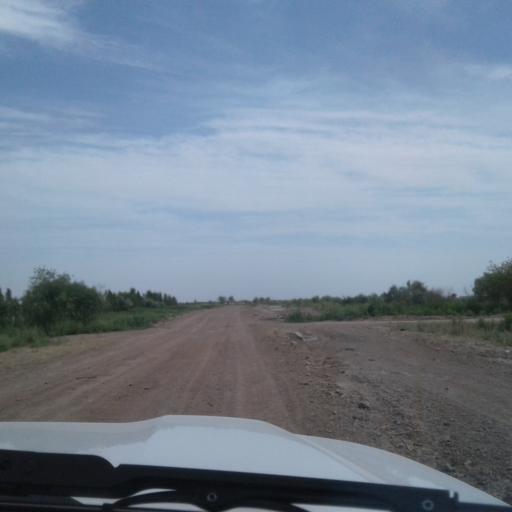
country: TM
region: Dasoguz
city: Tagta
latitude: 41.5494
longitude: 59.8121
